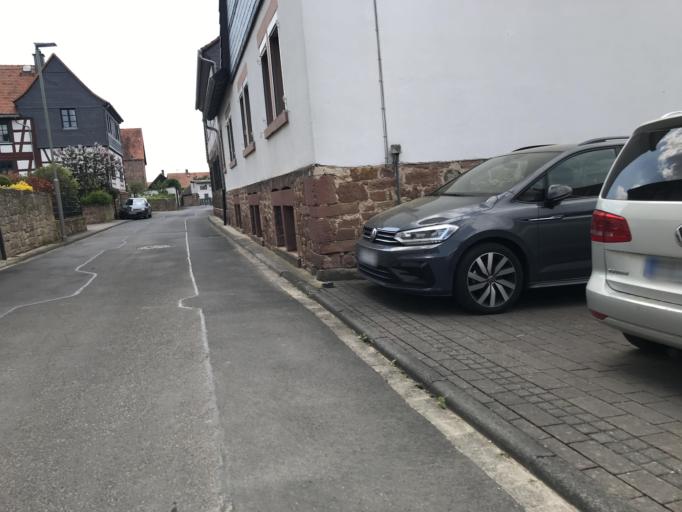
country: DE
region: Hesse
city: Ortenberg
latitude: 50.3156
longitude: 9.0703
